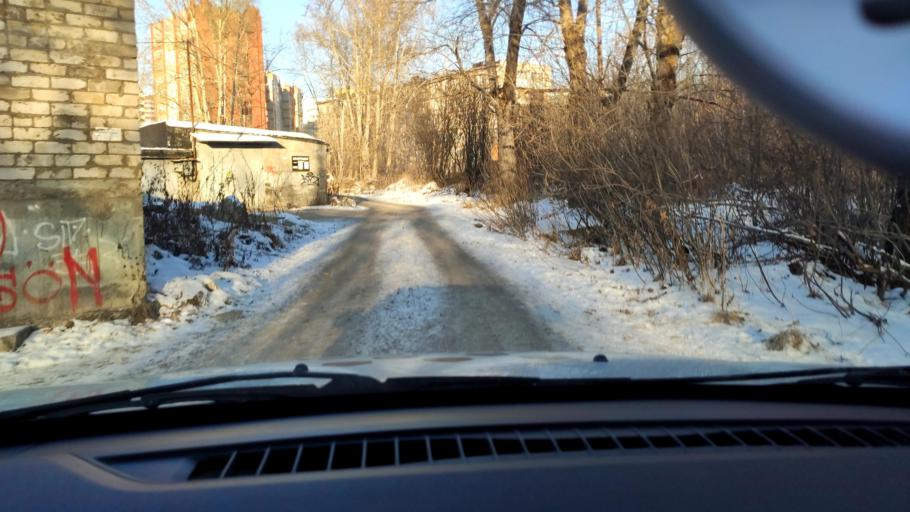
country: RU
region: Perm
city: Kondratovo
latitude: 58.0303
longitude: 56.0301
